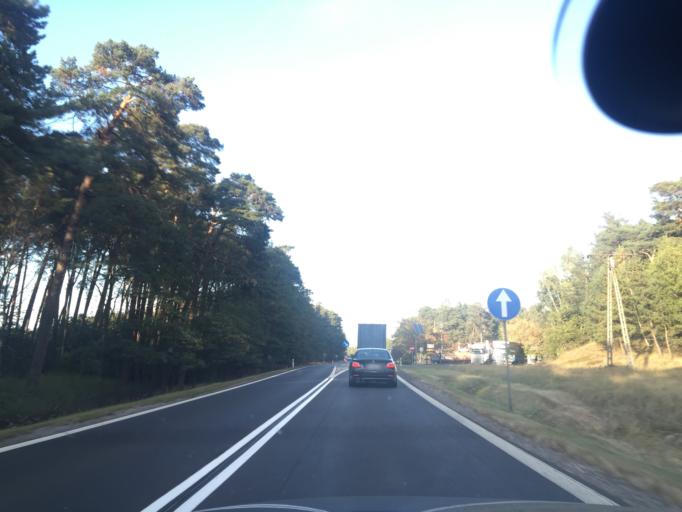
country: PL
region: Kujawsko-Pomorskie
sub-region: Powiat torunski
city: Wielka Nieszawka
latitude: 52.9532
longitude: 18.5295
